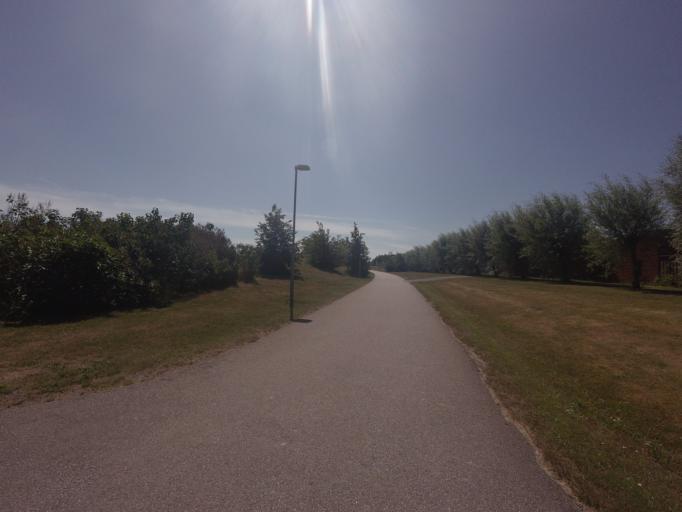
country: SE
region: Skane
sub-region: Vellinge Kommun
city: Hollviken
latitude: 55.4253
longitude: 12.9751
